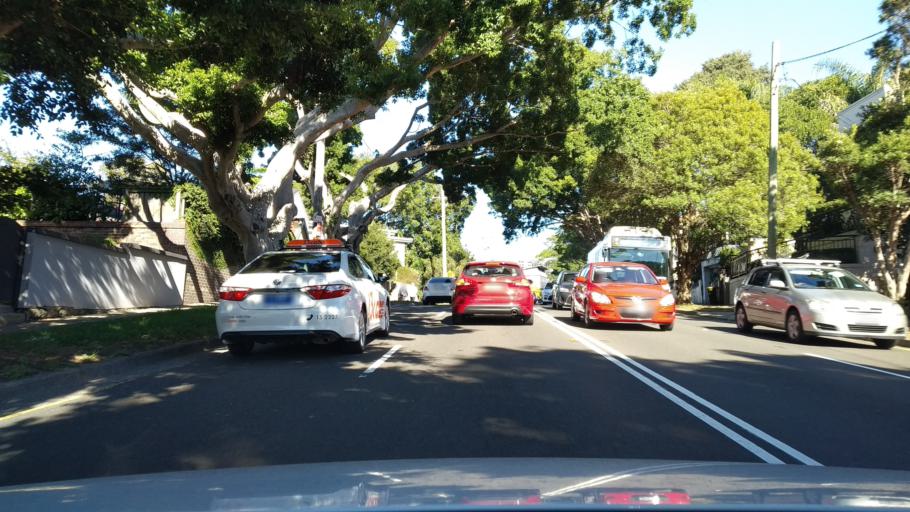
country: AU
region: New South Wales
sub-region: Waverley
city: Bondi Beach
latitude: -33.8865
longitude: 151.2665
